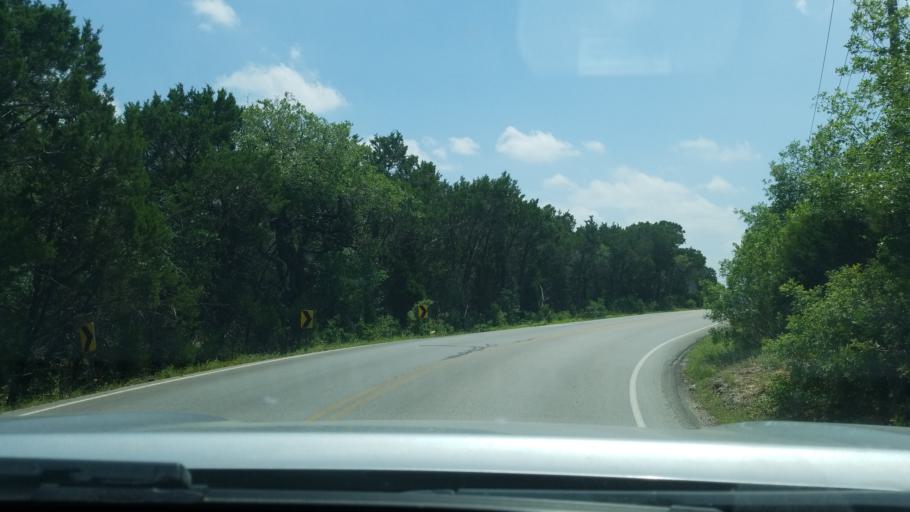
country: US
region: Texas
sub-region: Hays County
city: Woodcreek
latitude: 30.0231
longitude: -98.1301
